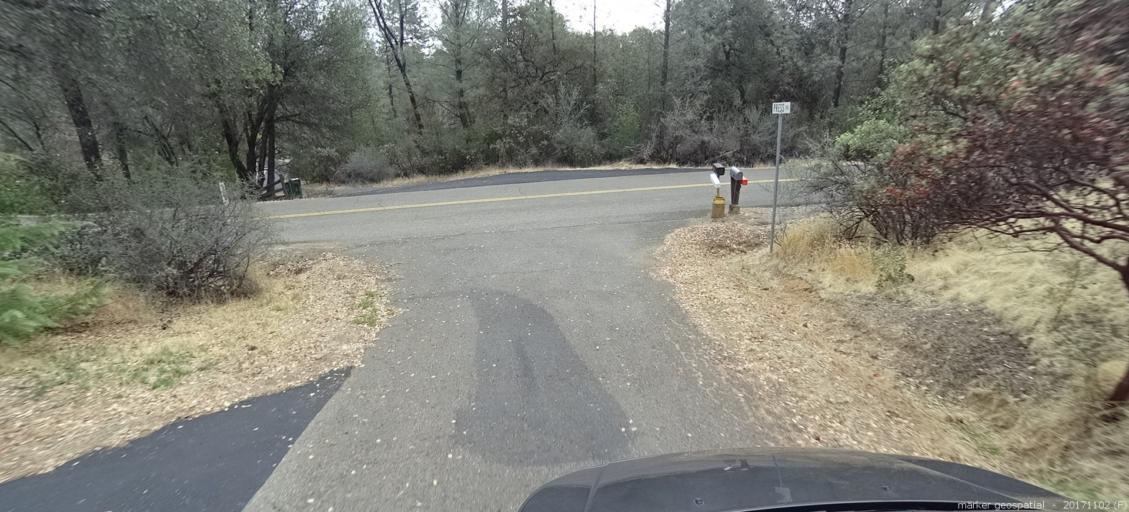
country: US
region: California
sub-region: Shasta County
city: Central Valley (historical)
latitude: 40.6593
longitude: -122.3994
